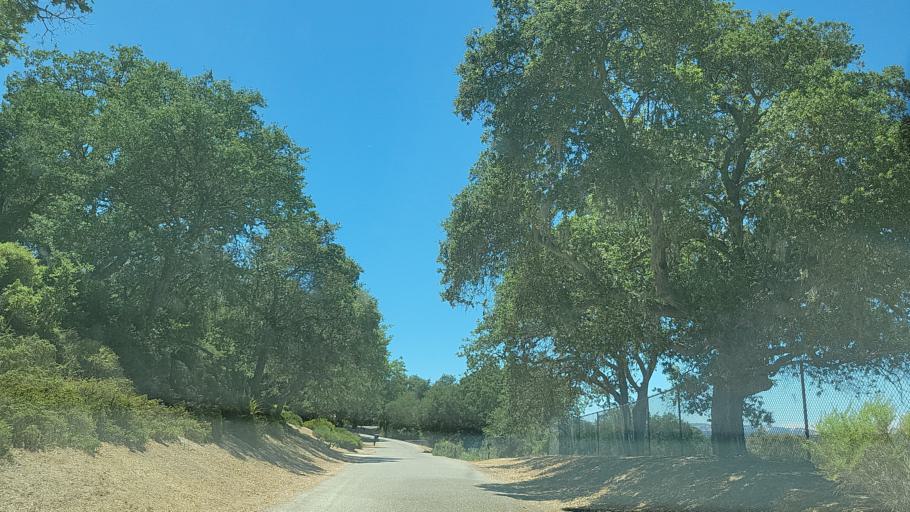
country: US
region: California
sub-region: San Luis Obispo County
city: Atascadero
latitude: 35.4692
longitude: -120.6454
